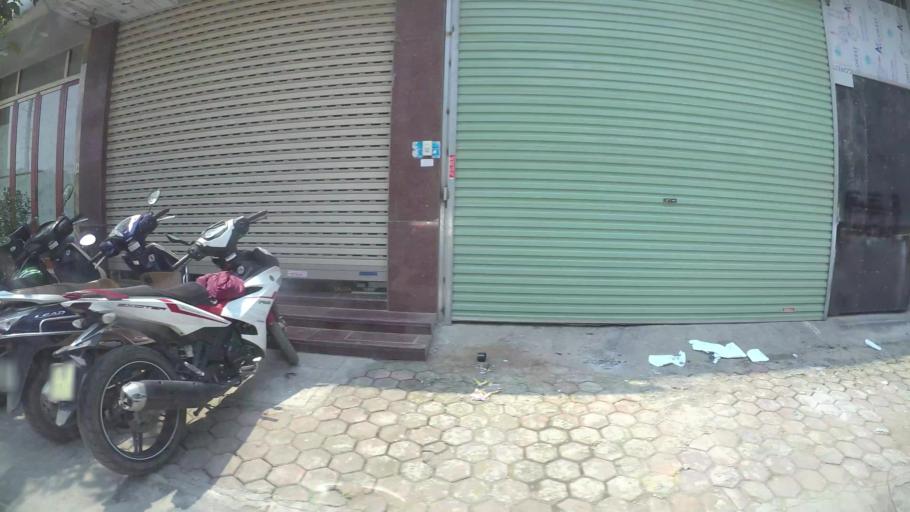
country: VN
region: Ha Noi
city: Ha Dong
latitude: 20.9844
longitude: 105.7725
